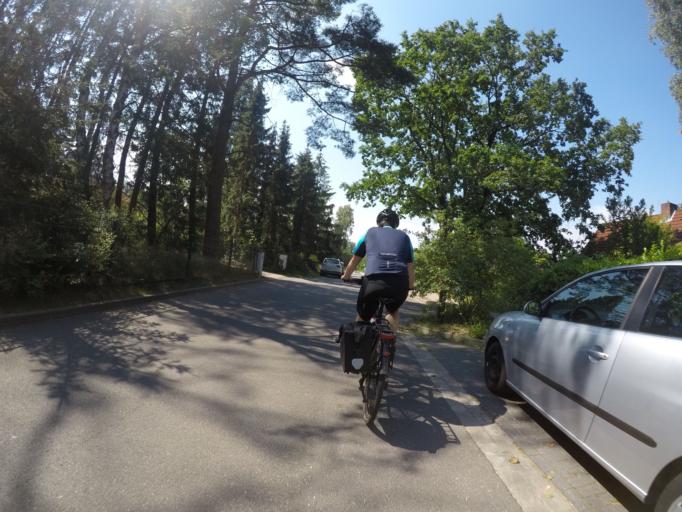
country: DE
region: Lower Saxony
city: Buchholz in der Nordheide
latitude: 53.3295
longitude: 9.8469
